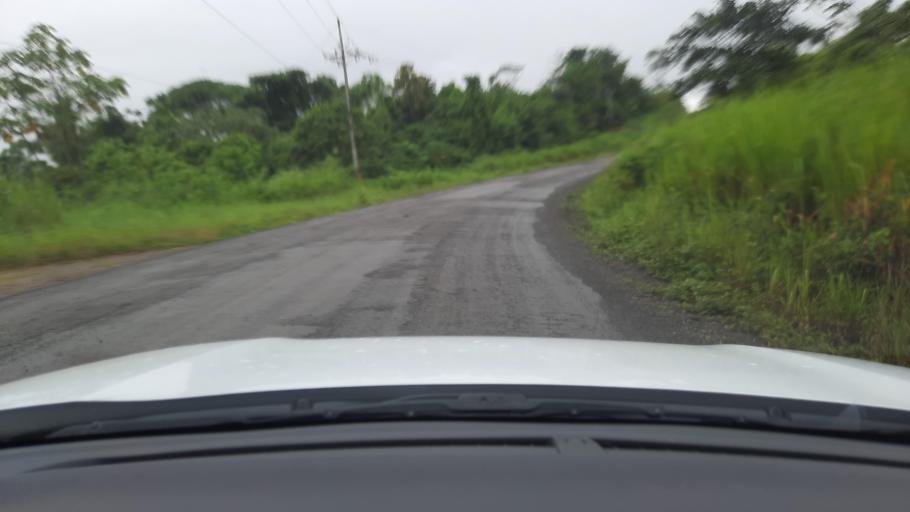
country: CR
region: Alajuela
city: San Jose
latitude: 11.0145
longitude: -85.3351
